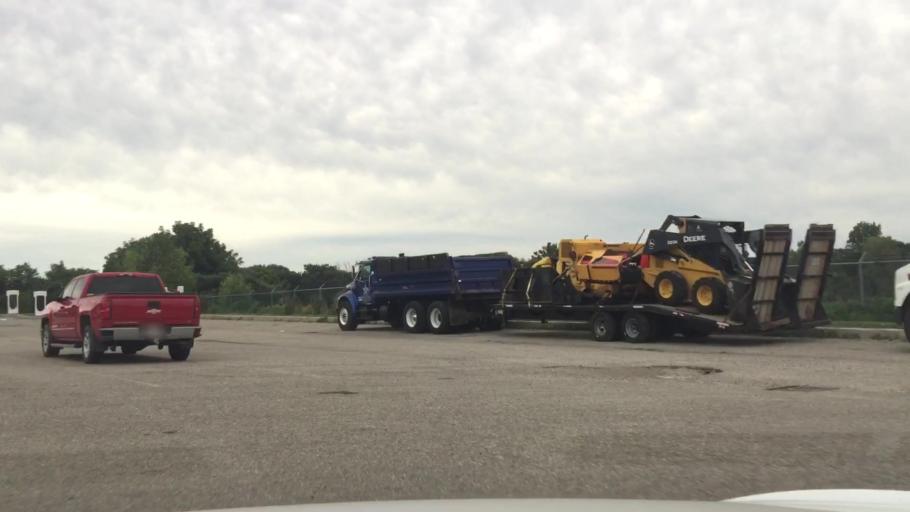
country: CA
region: Ontario
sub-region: Oxford County
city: Woodstock
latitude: 43.1125
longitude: -80.7389
